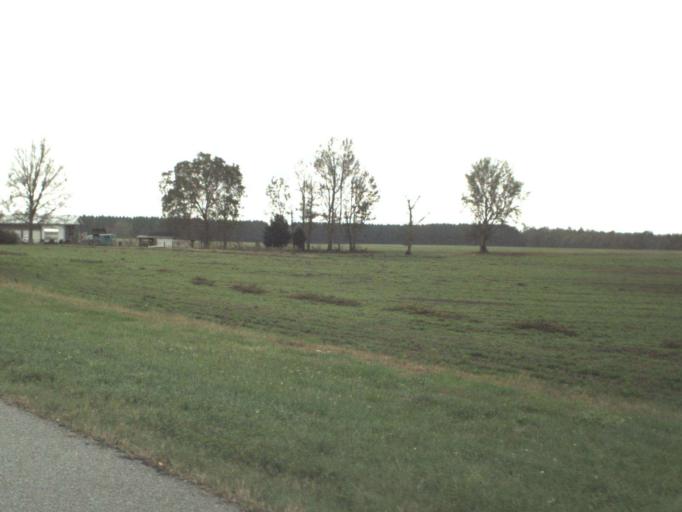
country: US
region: Alabama
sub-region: Escambia County
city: Atmore
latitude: 30.8735
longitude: -87.4439
